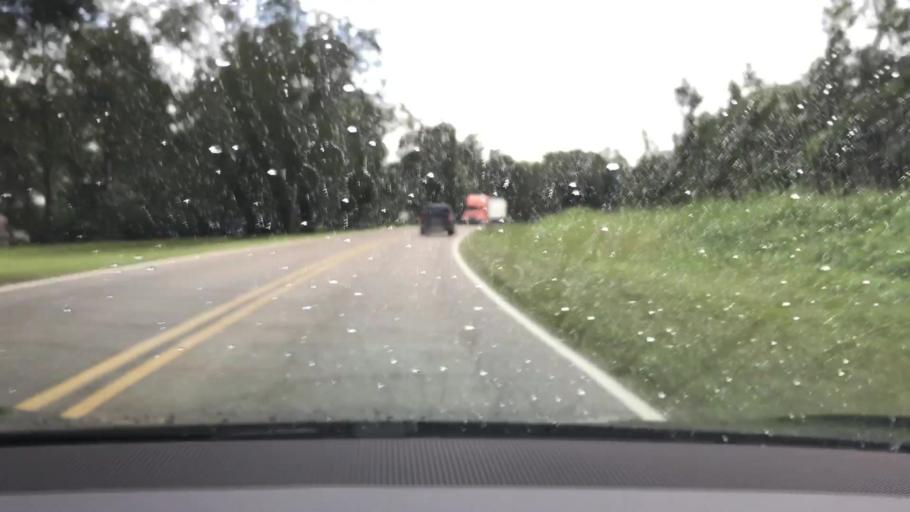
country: US
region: Alabama
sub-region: Geneva County
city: Samson
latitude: 31.1267
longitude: -86.1274
